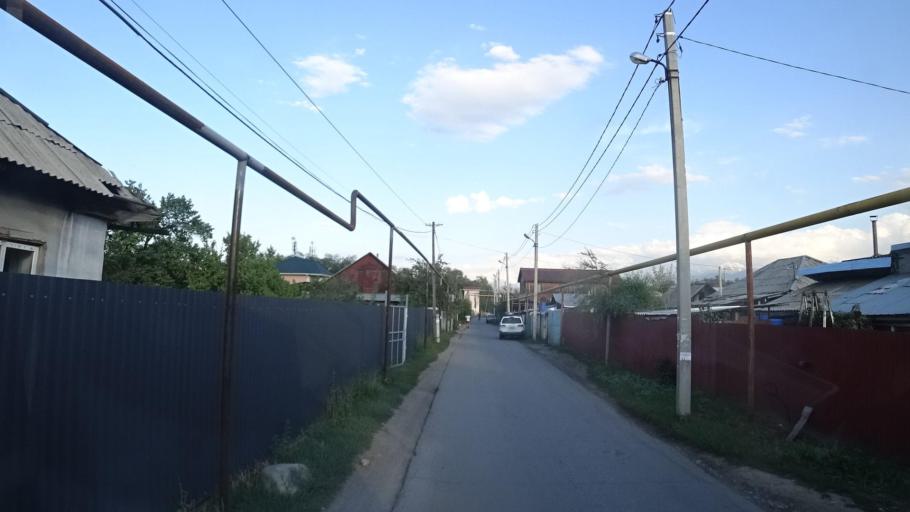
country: KZ
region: Almaty Oblysy
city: Pervomayskiy
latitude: 43.3325
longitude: 76.9914
